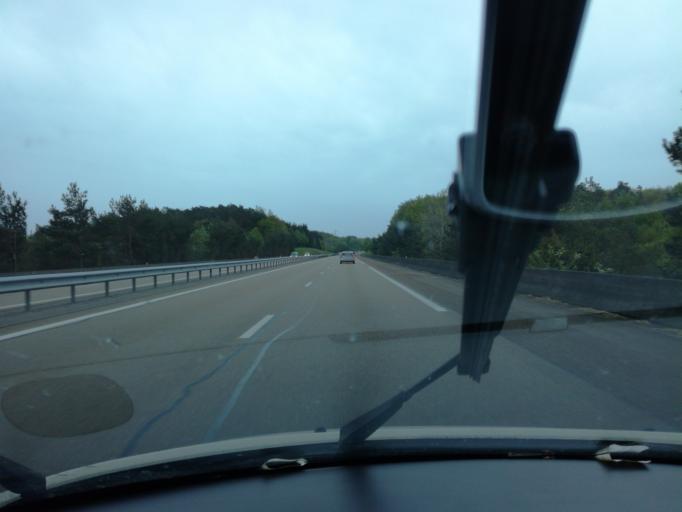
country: FR
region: Champagne-Ardenne
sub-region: Departement de la Haute-Marne
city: Chamarandes-Choignes
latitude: 48.0033
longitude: 5.1130
